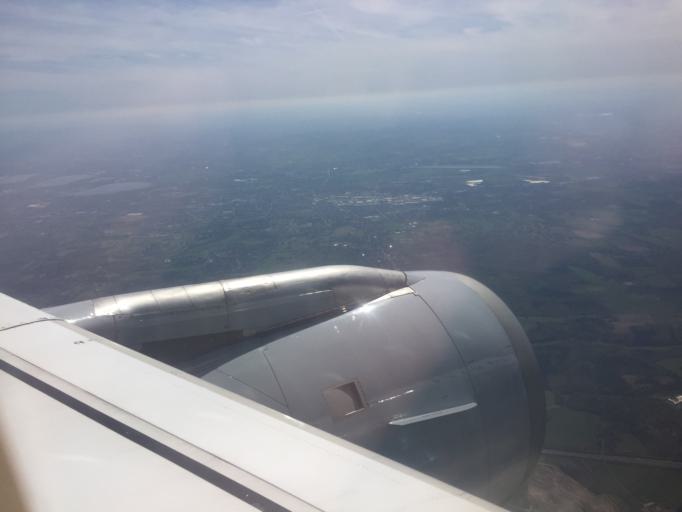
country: GB
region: England
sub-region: Buckinghamshire
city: Seer Green
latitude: 51.6129
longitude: -0.5909
